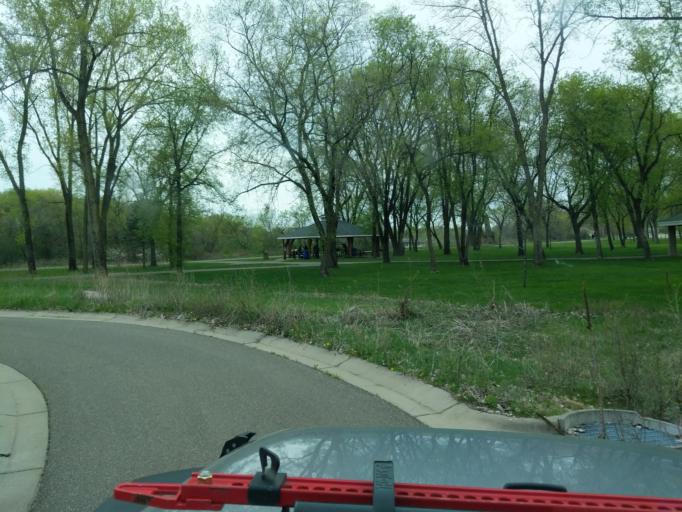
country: US
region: Minnesota
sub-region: Anoka County
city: Coon Rapids
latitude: 45.1463
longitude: -93.3052
